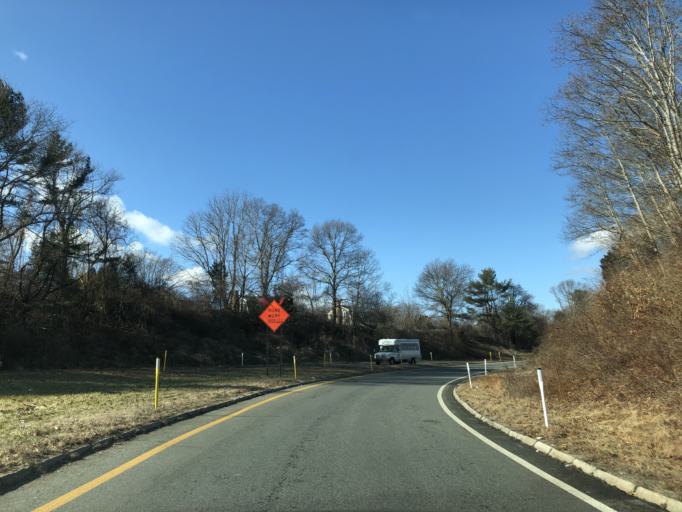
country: US
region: Massachusetts
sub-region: Bristol County
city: New Bedford
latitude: 41.6511
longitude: -70.9547
